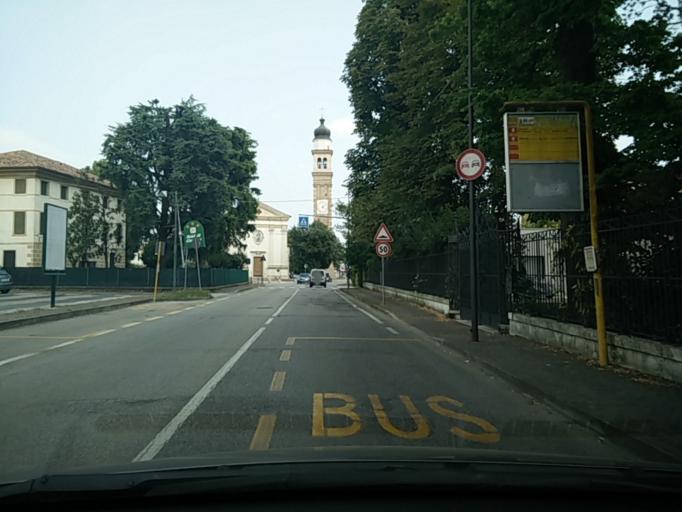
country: IT
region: Veneto
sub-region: Provincia di Treviso
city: Dosson
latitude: 45.6463
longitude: 12.2678
